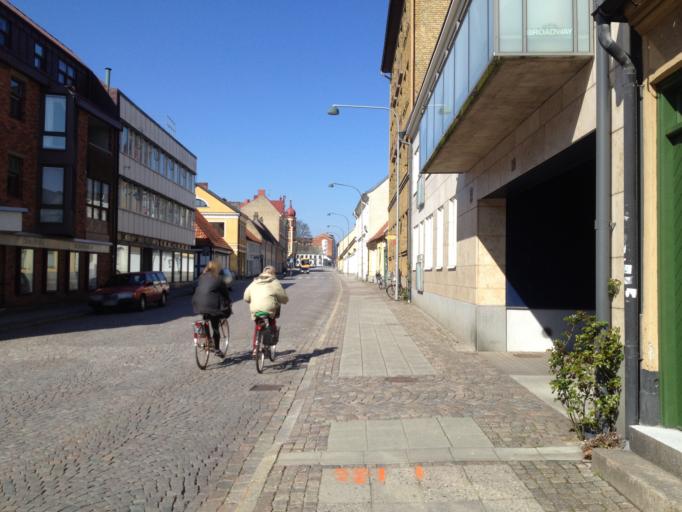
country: SE
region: Skane
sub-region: Lunds Kommun
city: Lund
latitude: 55.7074
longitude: 13.1928
